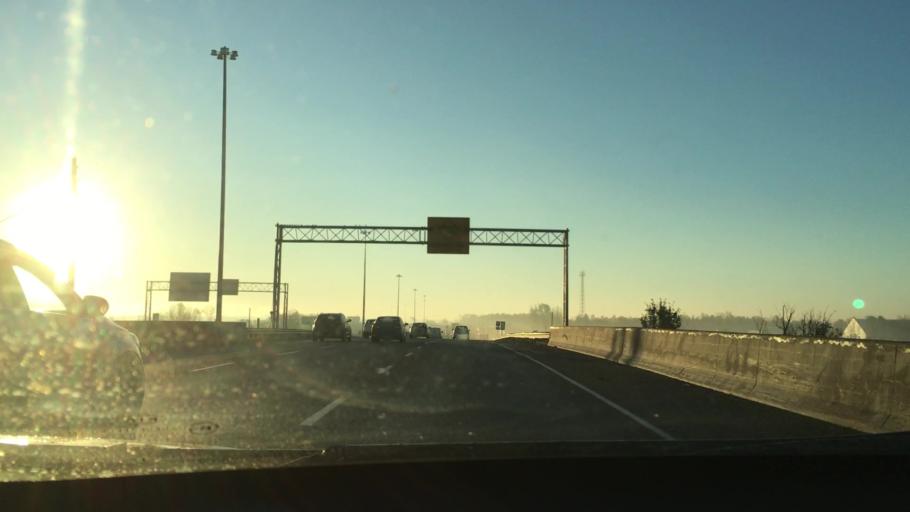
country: CA
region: Quebec
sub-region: Laurentides
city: Saint-Jerome
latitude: 45.7450
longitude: -74.0031
